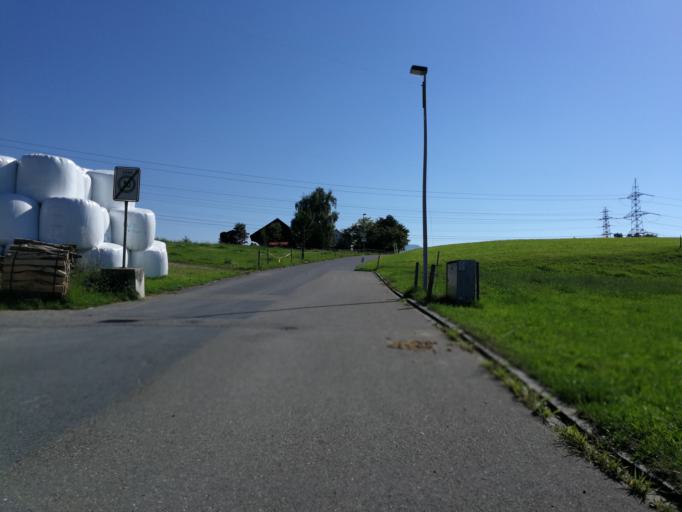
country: CH
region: Zurich
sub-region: Bezirk Hinwil
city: Wolfhausen
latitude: 47.2596
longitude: 8.8048
